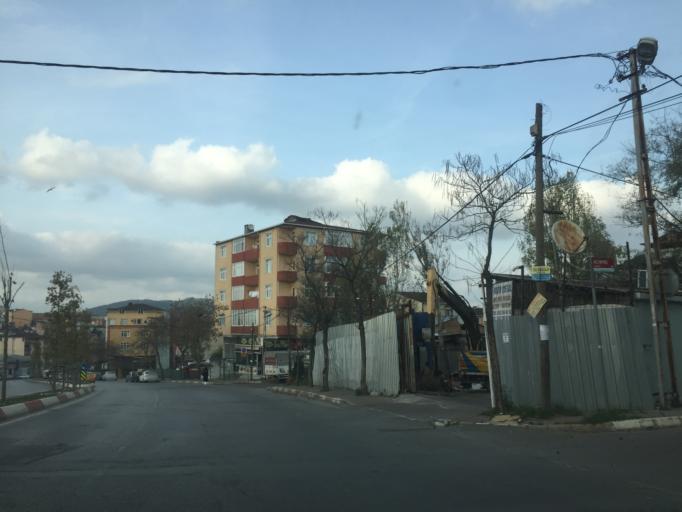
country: TR
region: Istanbul
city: Sultanbeyli
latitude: 40.9441
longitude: 29.3003
